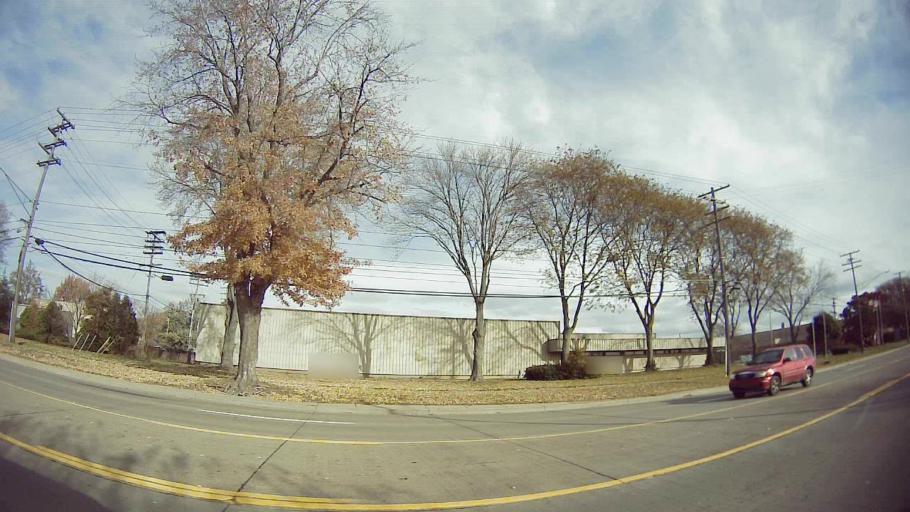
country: US
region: Michigan
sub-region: Macomb County
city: Warren
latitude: 42.4624
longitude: -83.0481
